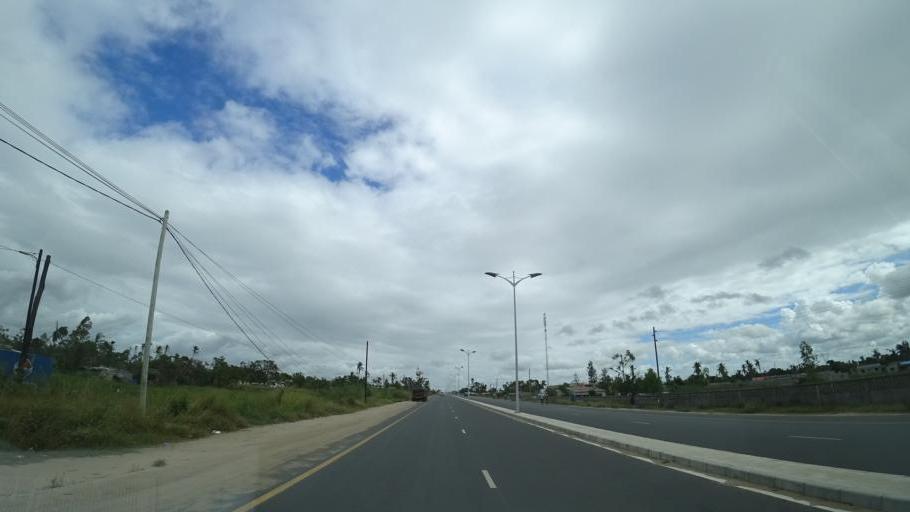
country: MZ
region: Sofala
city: Beira
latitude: -19.7338
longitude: 34.8294
